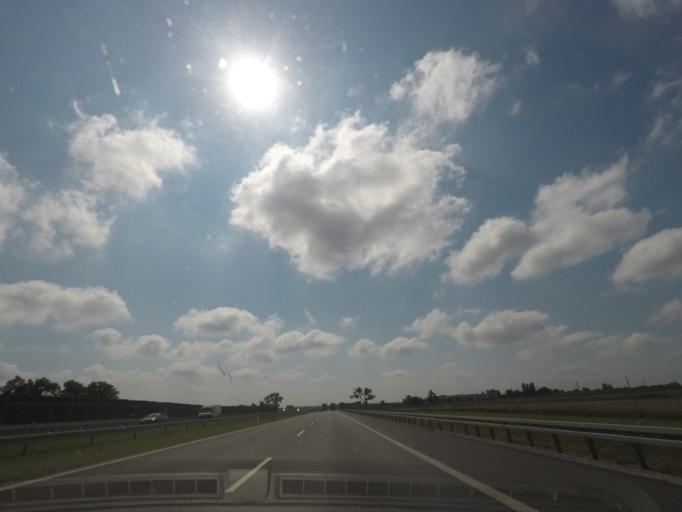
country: PL
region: Kujawsko-Pomorskie
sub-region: Powiat wloclawski
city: Brzesc Kujawski
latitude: 52.6335
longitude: 18.9551
